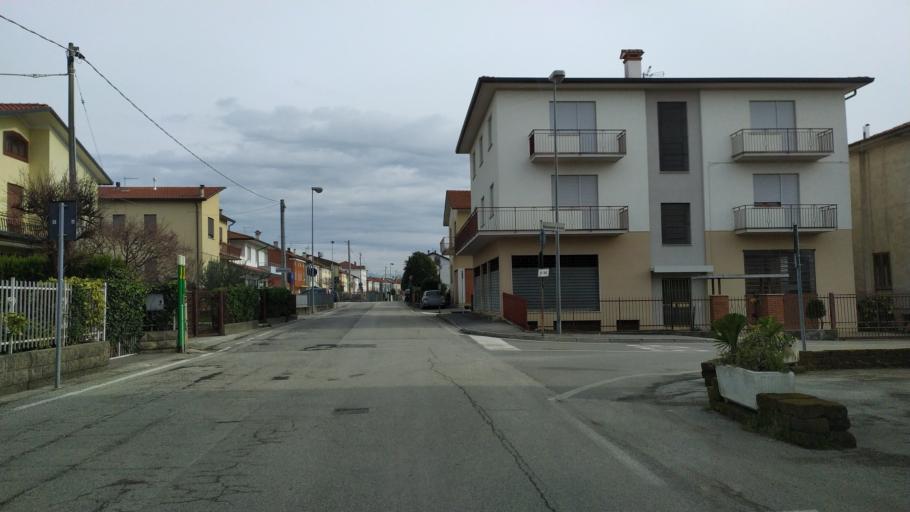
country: IT
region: Veneto
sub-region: Provincia di Vicenza
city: Villaverla
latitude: 45.6539
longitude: 11.4900
